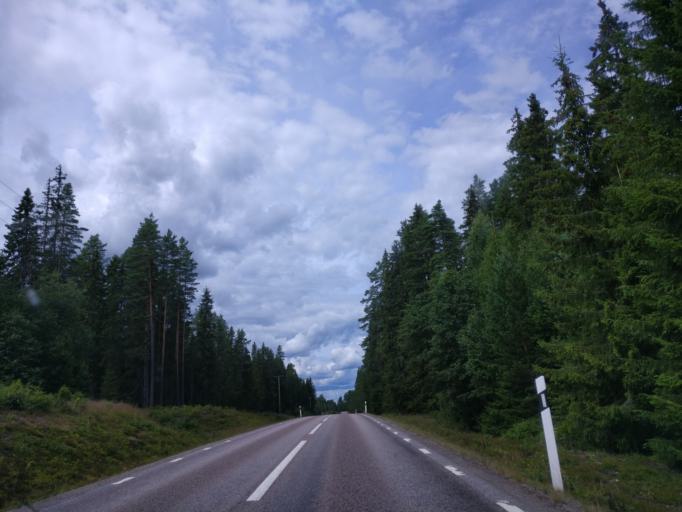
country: SE
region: Vaermland
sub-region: Hagfors Kommun
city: Ekshaerad
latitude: 60.1820
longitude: 13.3489
